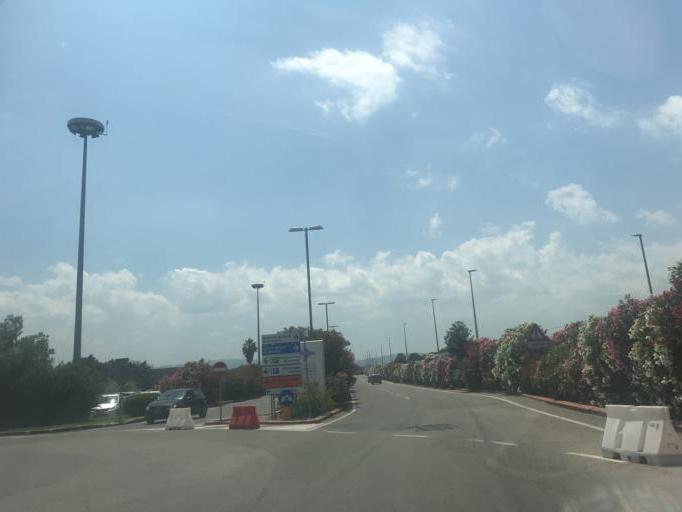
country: IT
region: Sardinia
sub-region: Provincia di Olbia-Tempio
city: Olbia
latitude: 40.9036
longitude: 9.5125
